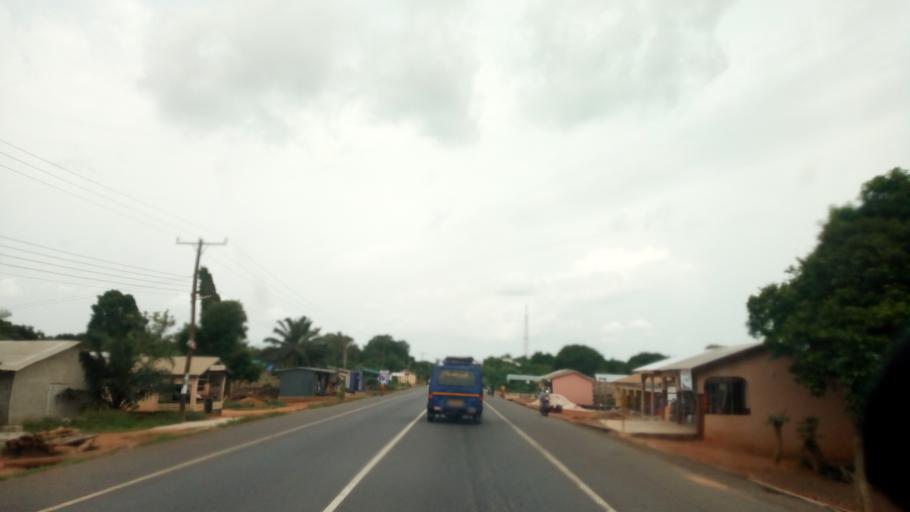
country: GH
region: Volta
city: Keta
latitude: 6.0641
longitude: 0.9107
